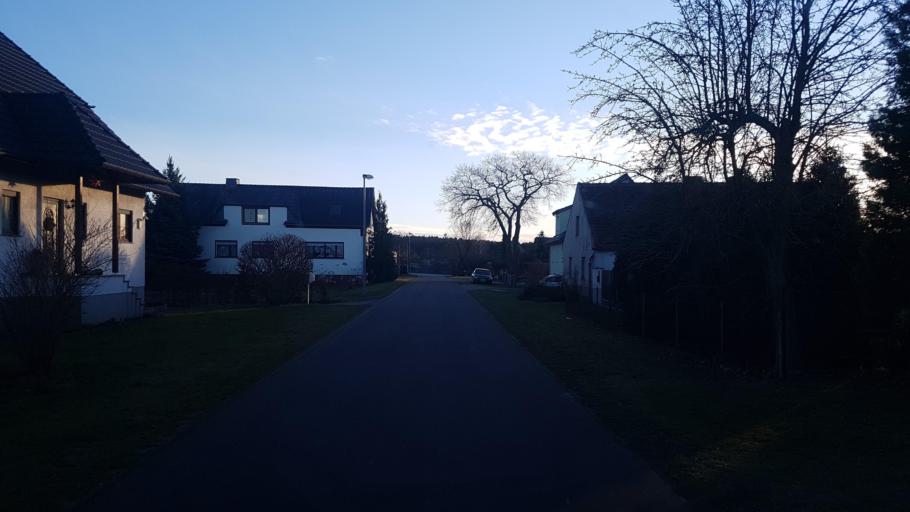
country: DE
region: Brandenburg
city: Drachhausen
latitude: 51.8847
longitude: 14.3196
